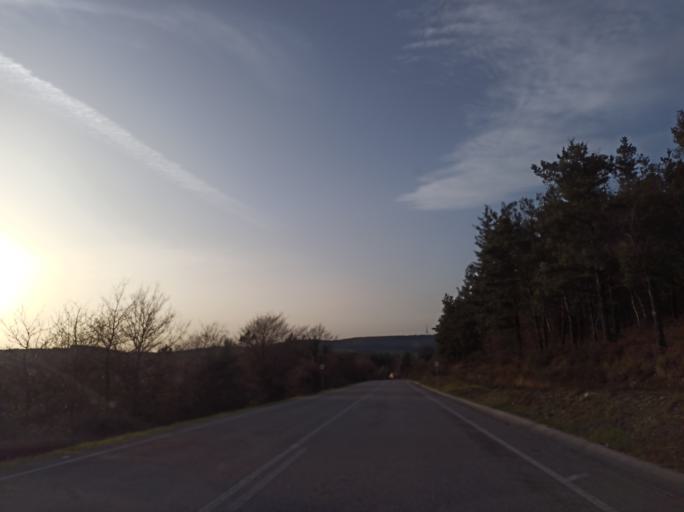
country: ES
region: Galicia
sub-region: Provincia de Lugo
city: Friol
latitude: 43.0350
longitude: -7.8932
